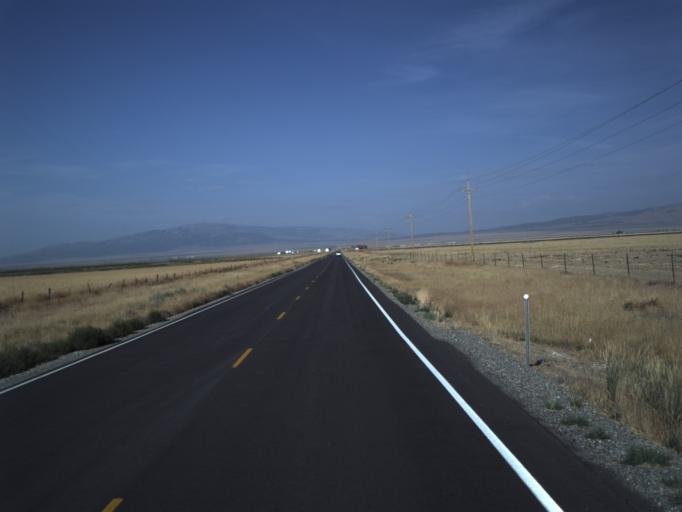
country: US
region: Idaho
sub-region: Oneida County
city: Malad City
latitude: 41.9672
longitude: -112.8443
